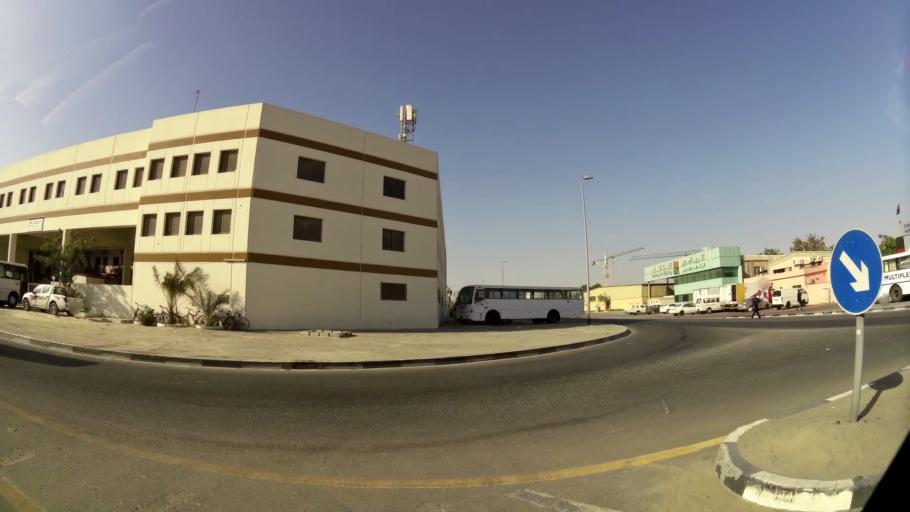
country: AE
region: Dubai
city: Dubai
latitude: 25.1207
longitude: 55.2306
